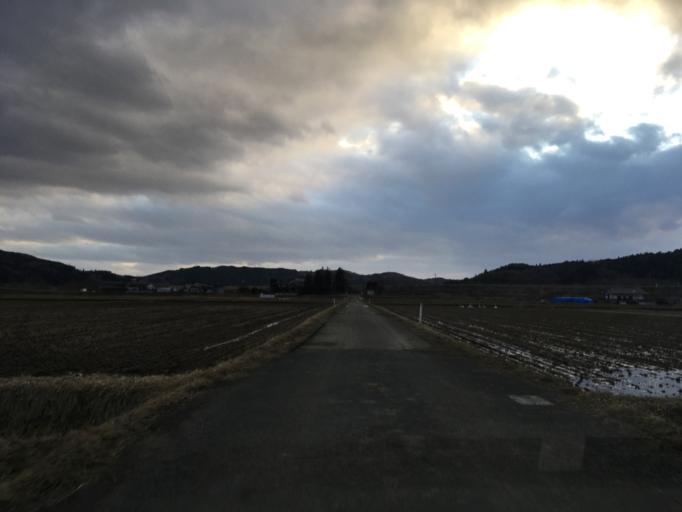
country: JP
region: Iwate
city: Ichinoseki
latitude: 38.8442
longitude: 141.2682
